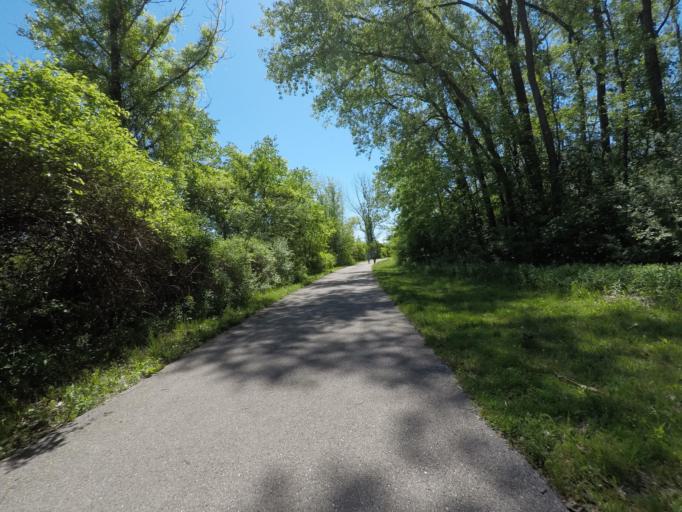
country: US
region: Wisconsin
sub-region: Sheboygan County
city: Kohler
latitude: 43.7528
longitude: -87.7685
